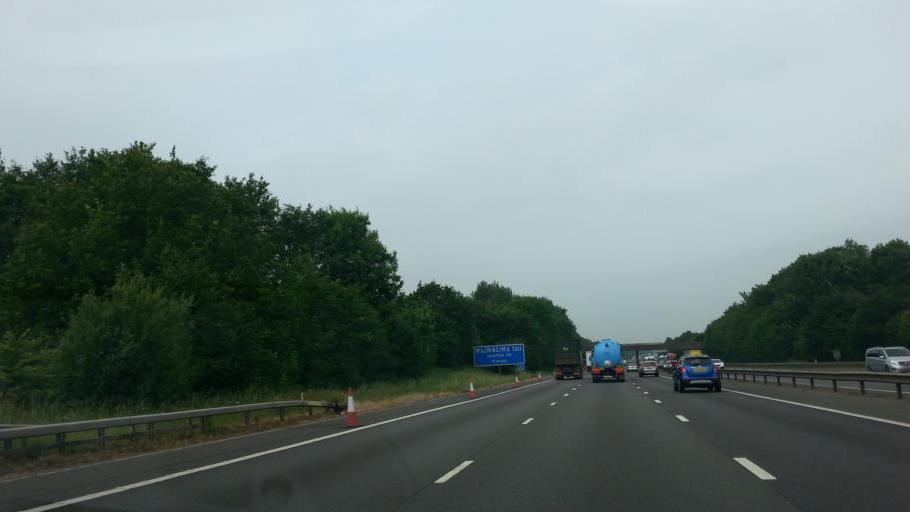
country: GB
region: England
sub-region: Coventry
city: Keresley
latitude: 52.4682
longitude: -1.5844
